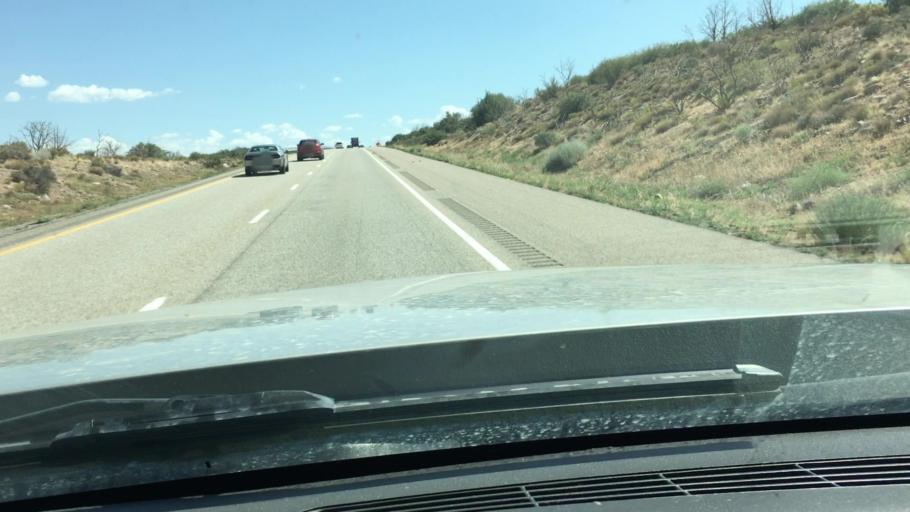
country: US
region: Utah
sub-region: Washington County
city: Toquerville
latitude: 37.3005
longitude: -113.2994
